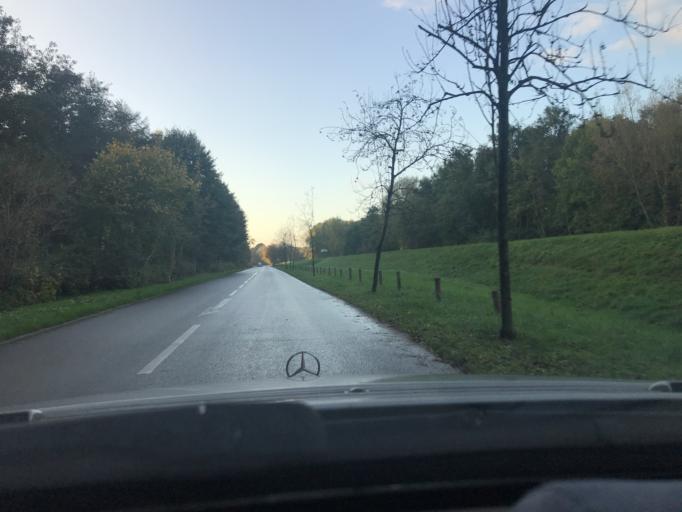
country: DE
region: Mecklenburg-Vorpommern
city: Koserow
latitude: 54.0590
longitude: 13.9953
